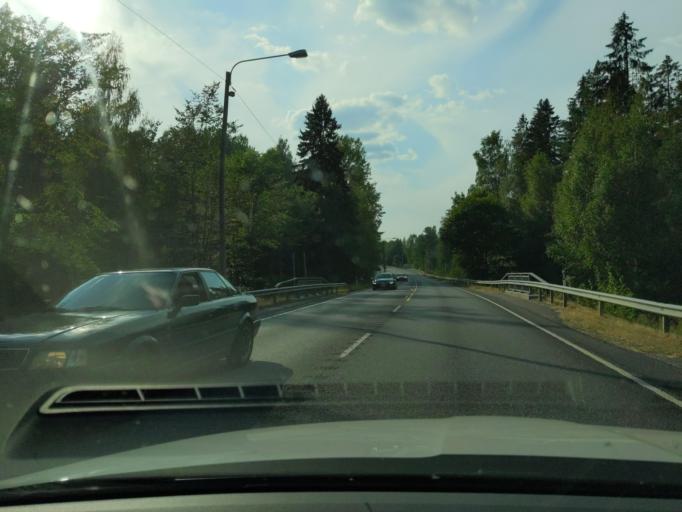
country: FI
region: Paijanne Tavastia
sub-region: Lahti
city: Asikkala
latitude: 61.1685
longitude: 25.5568
